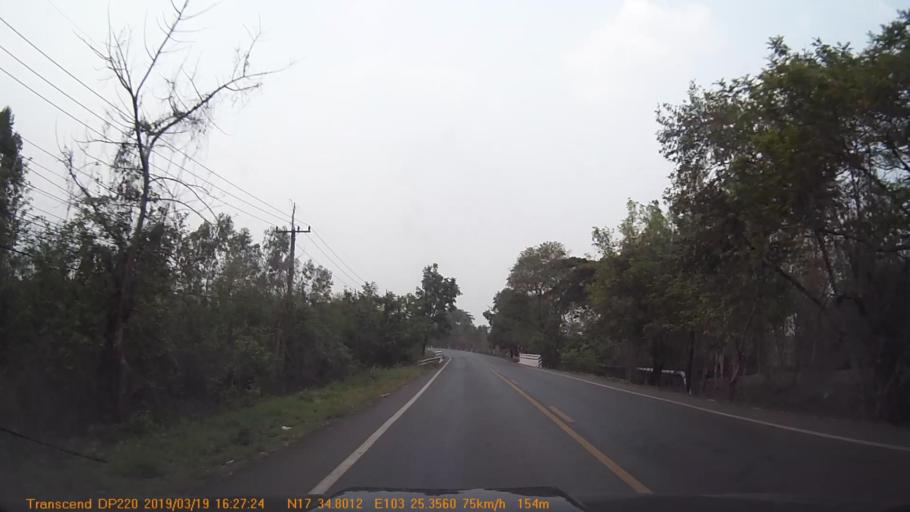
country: TH
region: Sakon Nakhon
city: Sawang Daen Din
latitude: 17.5808
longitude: 103.4230
